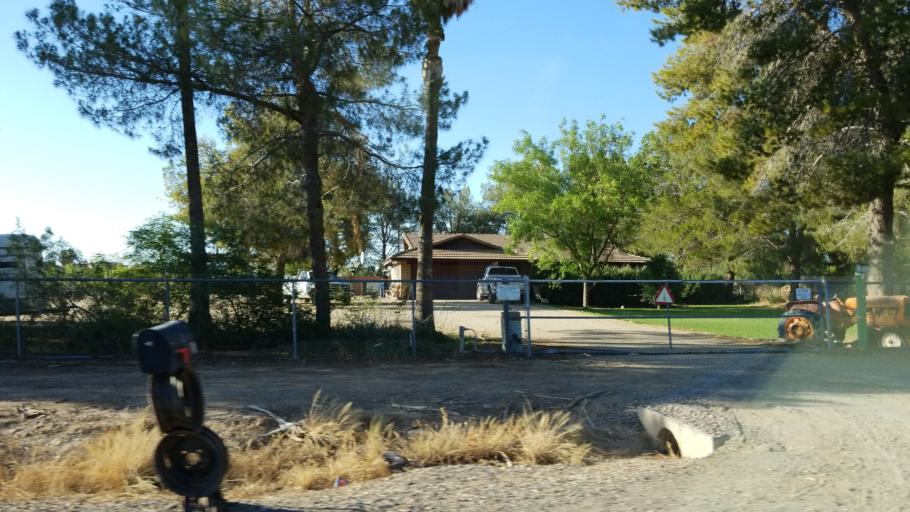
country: US
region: Arizona
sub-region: Maricopa County
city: Laveen
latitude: 33.3774
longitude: -112.2064
